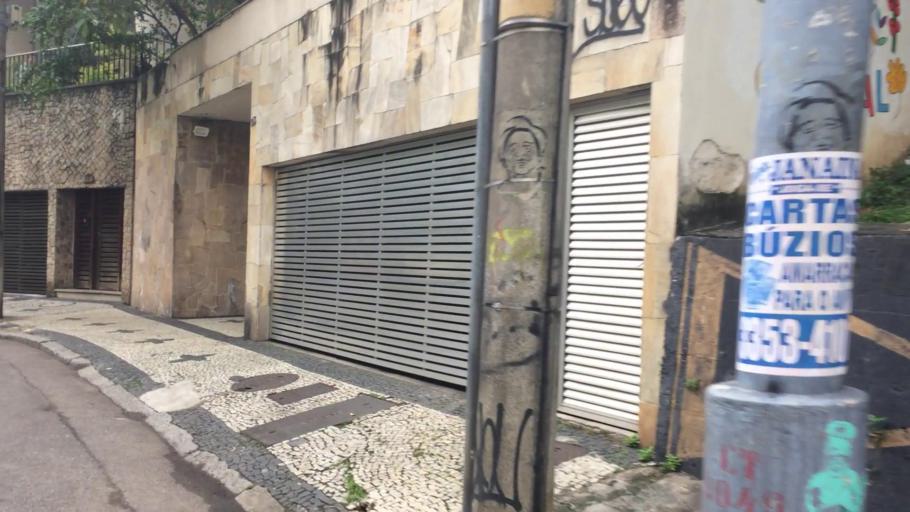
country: BR
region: Rio de Janeiro
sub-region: Rio De Janeiro
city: Rio de Janeiro
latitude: -22.9430
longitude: -43.1910
